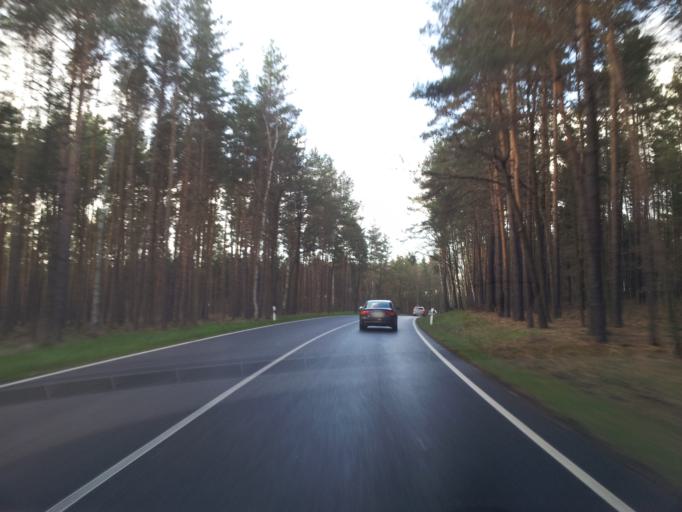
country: DE
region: Saxony
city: Konigsbruck
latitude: 51.2744
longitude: 13.9075
